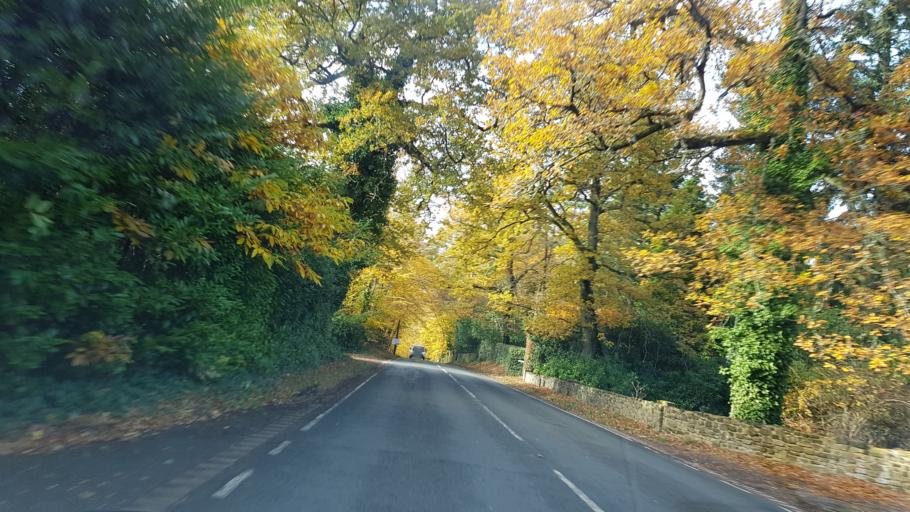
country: GB
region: England
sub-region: Surrey
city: Elstead
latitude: 51.1926
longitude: -0.7300
